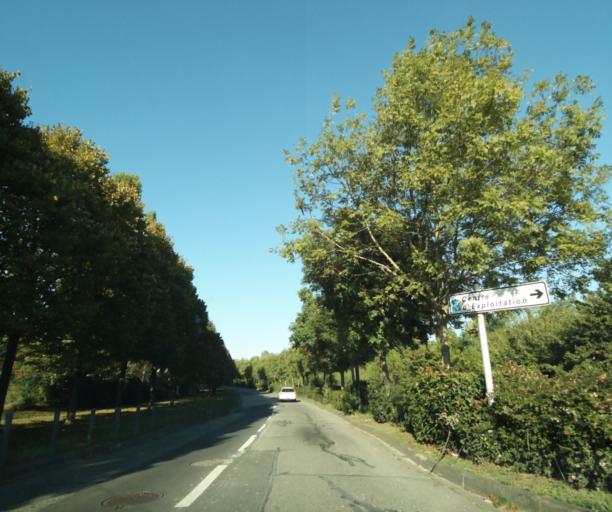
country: FR
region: Midi-Pyrenees
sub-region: Departement de la Haute-Garonne
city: Ramonville-Saint-Agne
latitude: 43.5741
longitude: 1.4947
